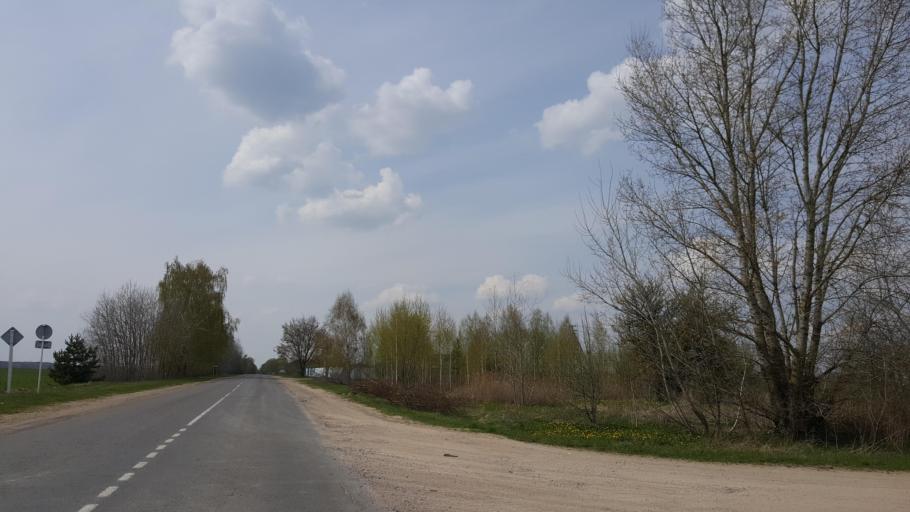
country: BY
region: Brest
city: Zhabinka
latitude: 52.2049
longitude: 23.9947
